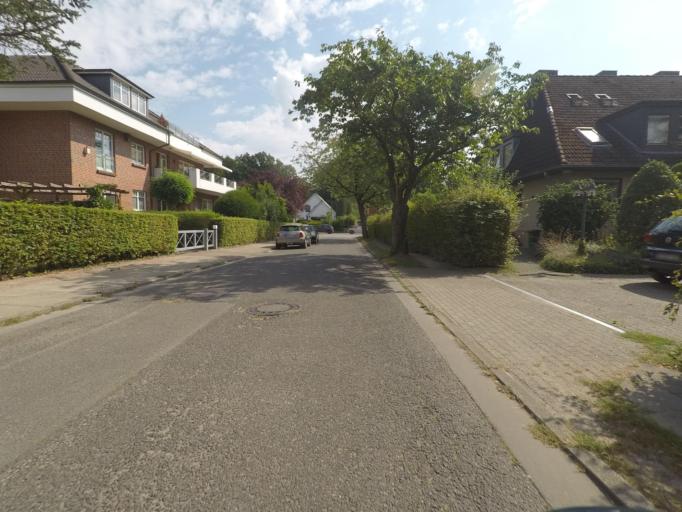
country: DE
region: Hamburg
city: Steilshoop
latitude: 53.6301
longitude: 10.0627
